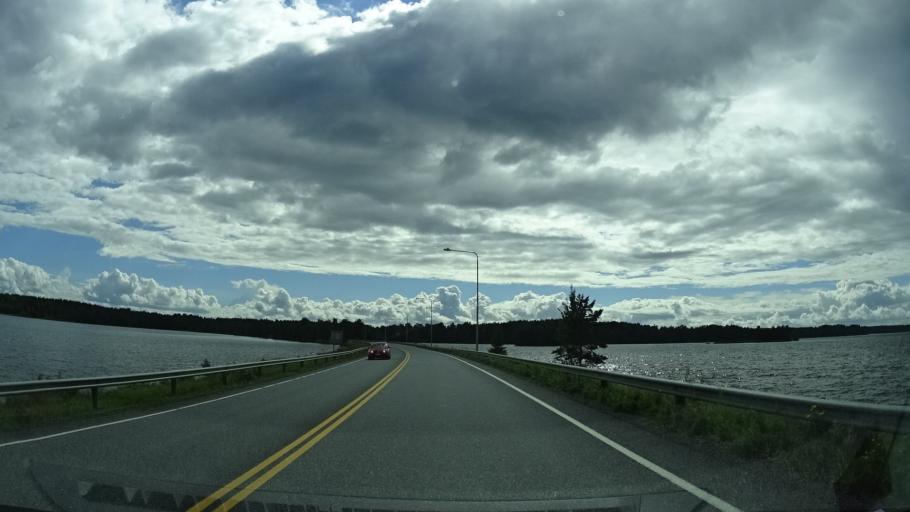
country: FI
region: Pirkanmaa
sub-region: Etelae-Pirkanmaa
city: Valkeakoski
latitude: 61.1800
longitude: 24.0376
